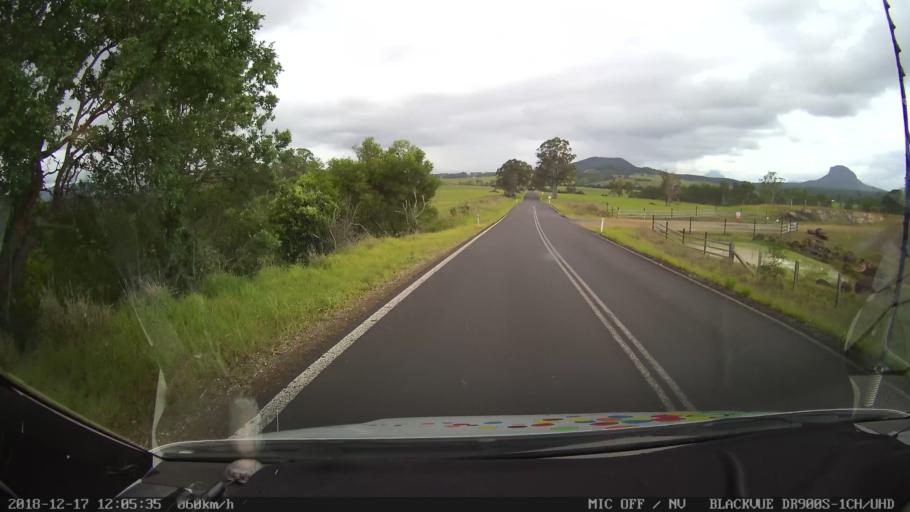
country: AU
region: New South Wales
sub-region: Kyogle
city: Kyogle
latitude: -28.4911
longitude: 152.5665
